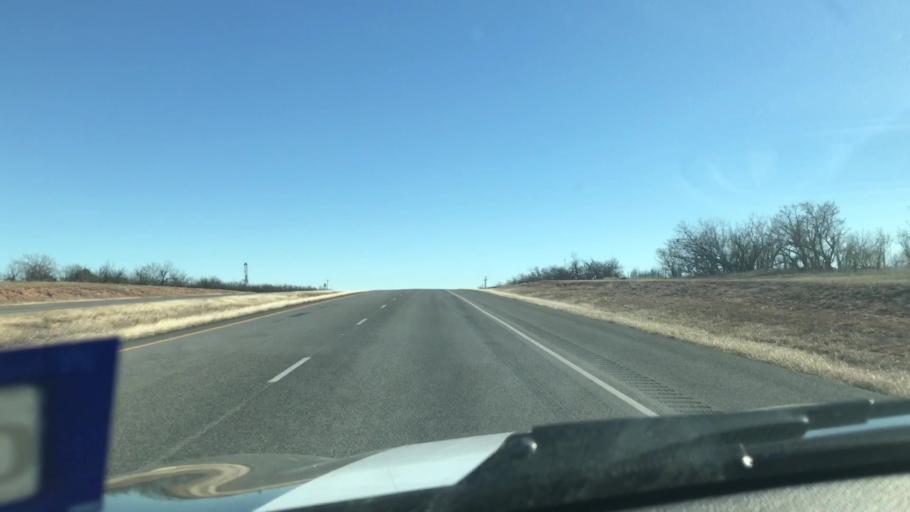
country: US
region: Texas
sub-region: Scurry County
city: Snyder
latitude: 32.7590
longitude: -100.9309
